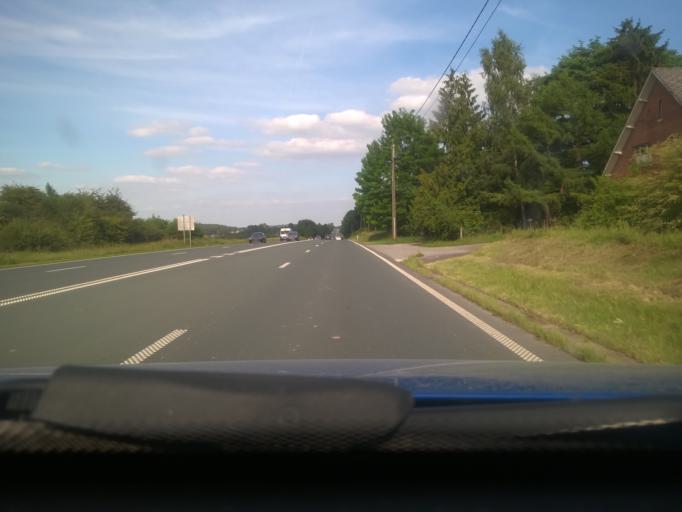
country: BE
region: Wallonia
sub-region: Province de Namur
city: Couvin
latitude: 50.0511
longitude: 4.4646
